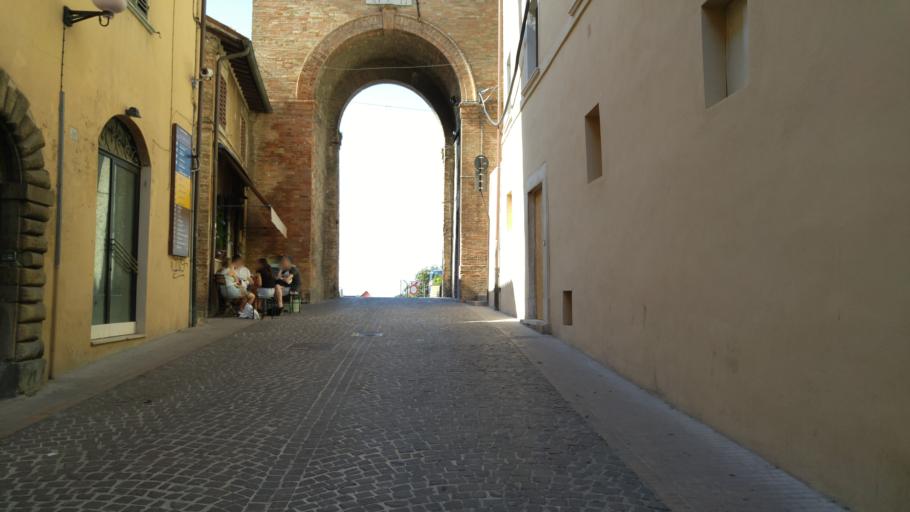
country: IT
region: The Marches
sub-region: Provincia di Pesaro e Urbino
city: Urbino
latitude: 43.7292
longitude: 12.6360
